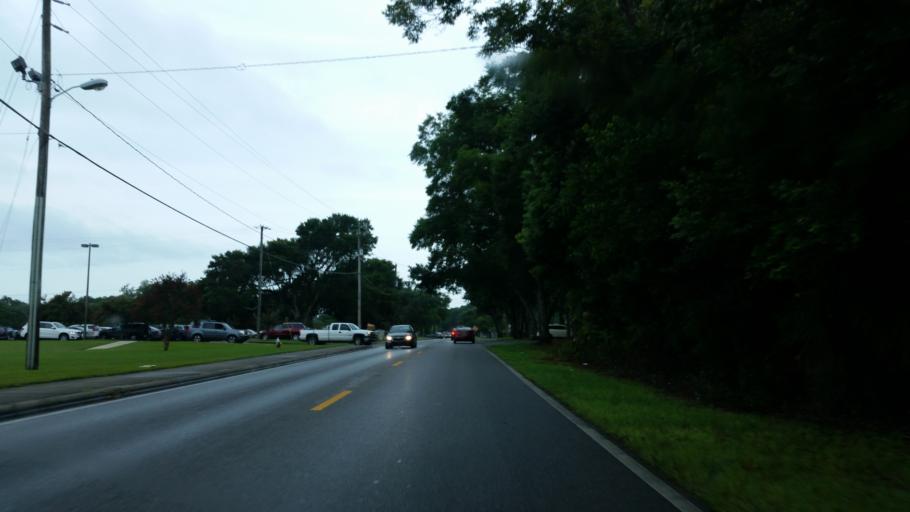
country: US
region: Florida
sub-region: Escambia County
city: Goulding
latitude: 30.4381
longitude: -87.2514
